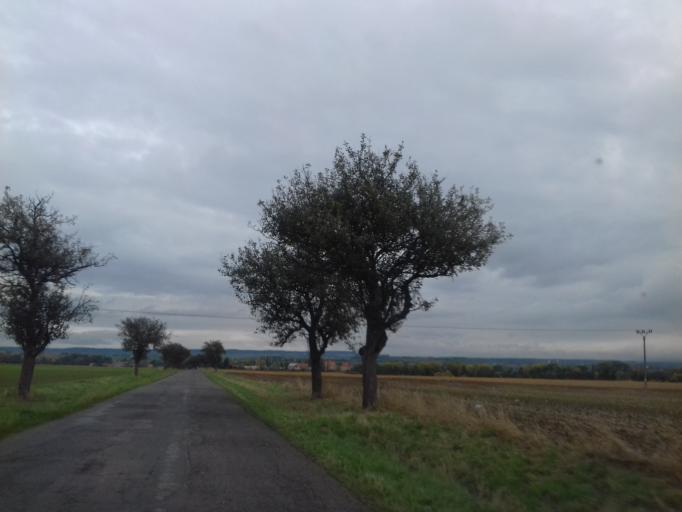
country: CZ
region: Pardubicky
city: Hrochuv Tynec
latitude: 49.9230
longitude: 15.8910
